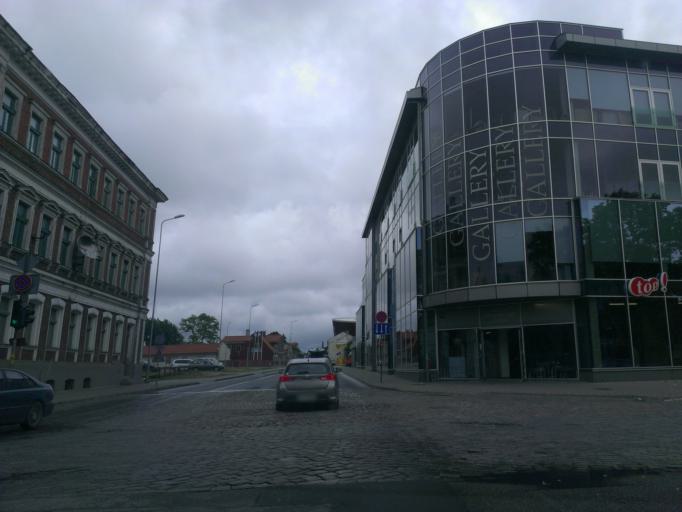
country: LV
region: Liepaja
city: Liepaja
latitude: 56.5109
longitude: 21.0056
